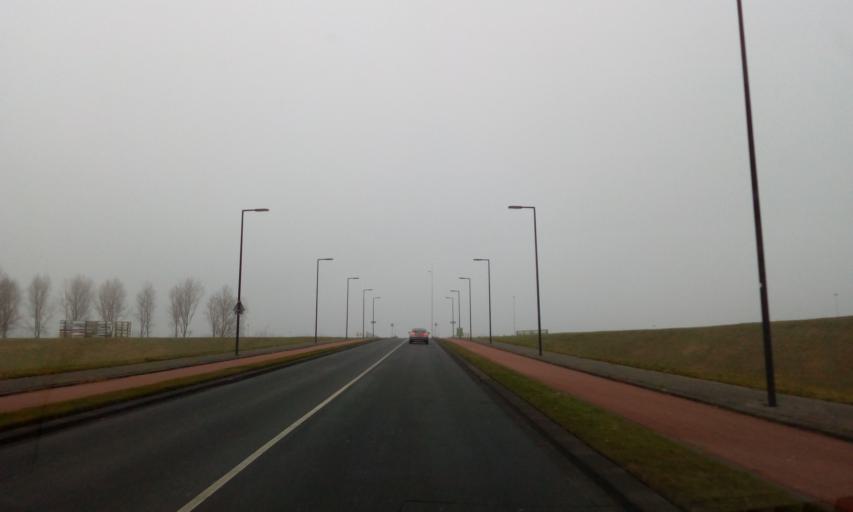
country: NL
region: South Holland
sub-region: Gemeente Capelle aan den IJssel
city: Capelle aan den IJssel
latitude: 51.9695
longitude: 4.5903
